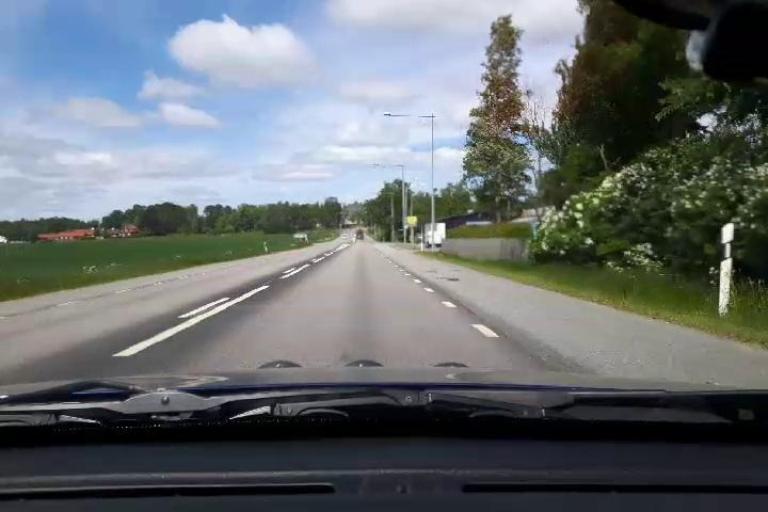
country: SE
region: Uppsala
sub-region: Osthammars Kommun
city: Bjorklinge
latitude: 60.0223
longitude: 17.5547
